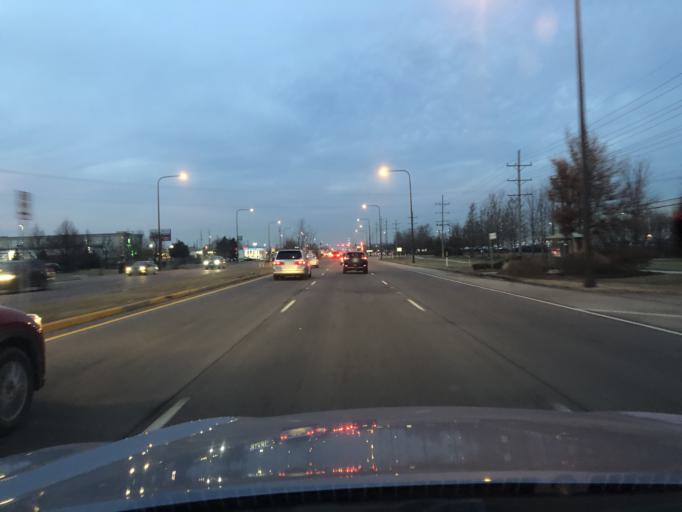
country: US
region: Illinois
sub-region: Cook County
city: Elk Grove Village
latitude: 42.0083
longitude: -87.9595
